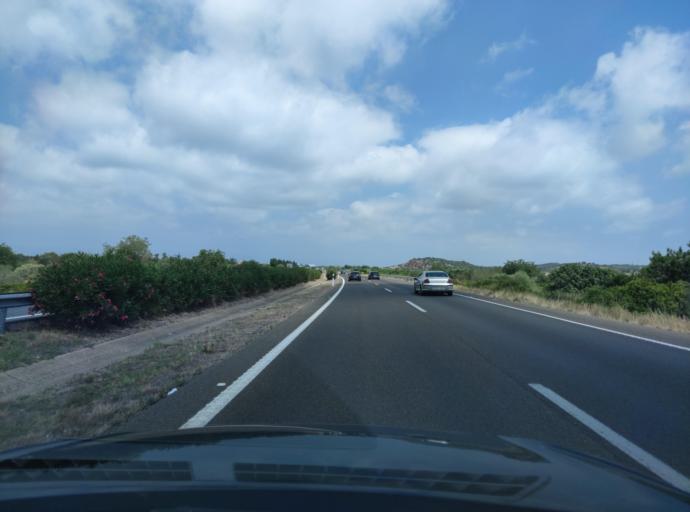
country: ES
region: Valencia
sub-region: Provincia de Castello
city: Vinaros
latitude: 40.4798
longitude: 0.4186
